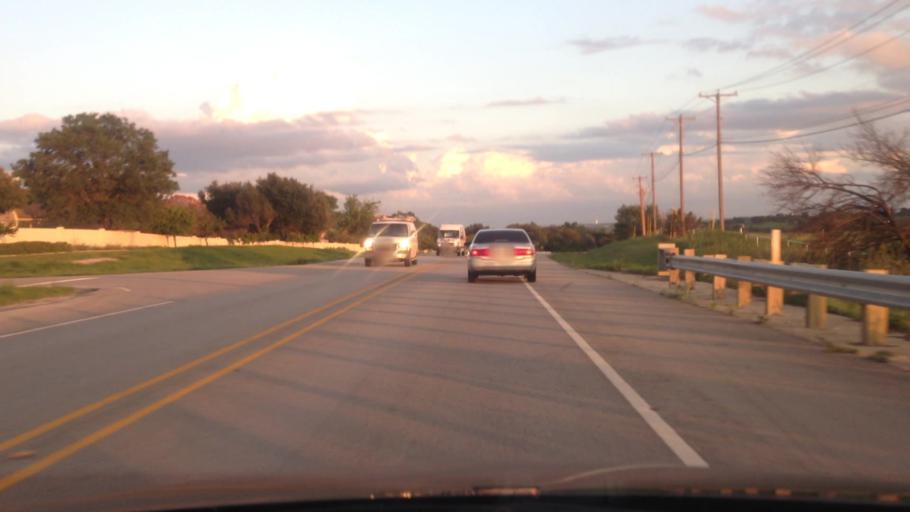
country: US
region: Texas
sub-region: Tarrant County
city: Benbrook
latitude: 32.6698
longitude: -97.4921
